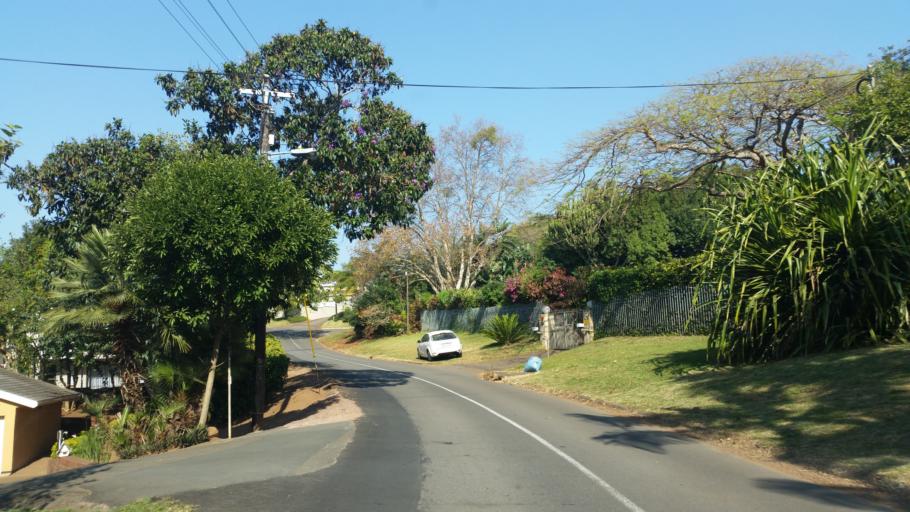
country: ZA
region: KwaZulu-Natal
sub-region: eThekwini Metropolitan Municipality
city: Berea
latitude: -29.8508
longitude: 30.9007
